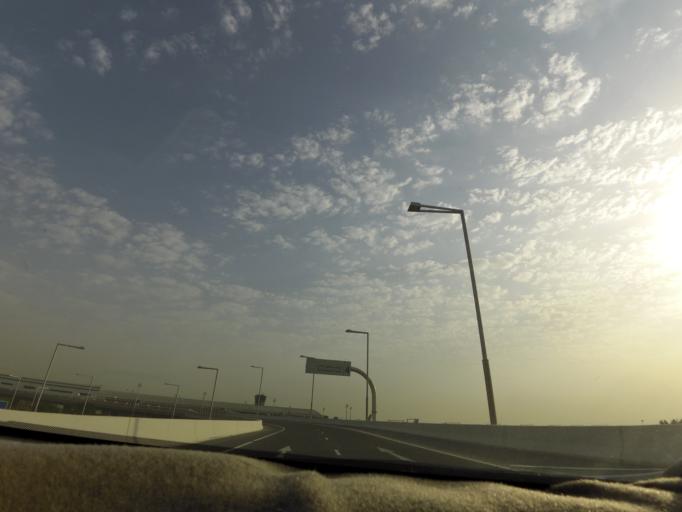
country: QA
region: Al Wakrah
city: Al Wakrah
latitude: 25.2591
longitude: 51.6172
